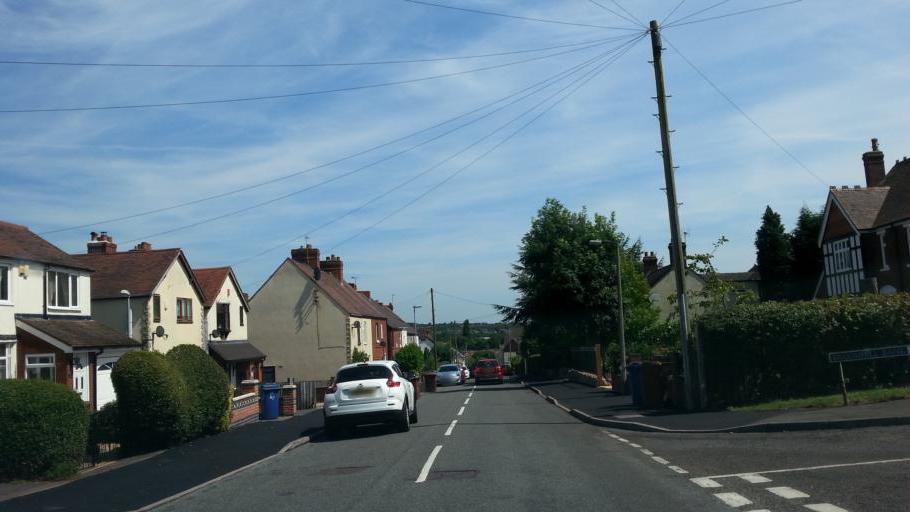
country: GB
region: England
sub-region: Staffordshire
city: Cannock
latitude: 52.7006
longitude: -2.0239
